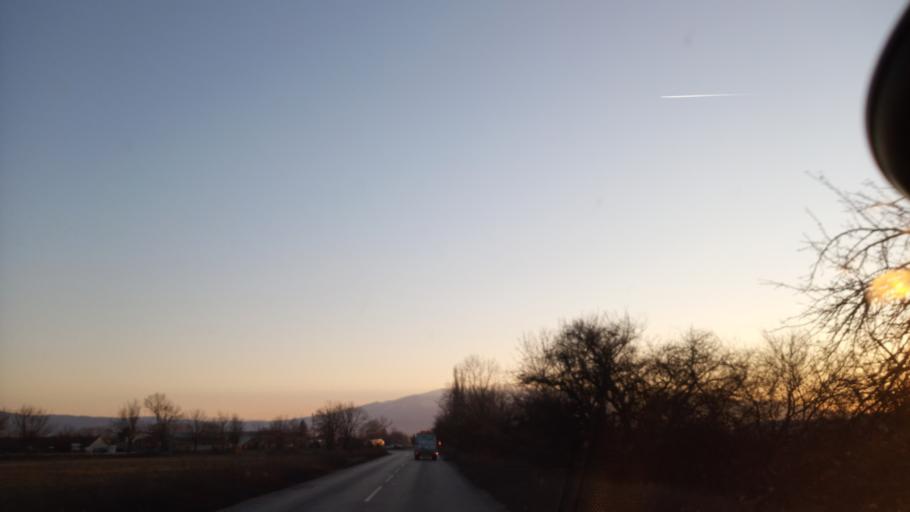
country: BG
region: Sofia-Capital
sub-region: Stolichna Obshtina
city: Bukhovo
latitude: 42.7395
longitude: 23.4709
